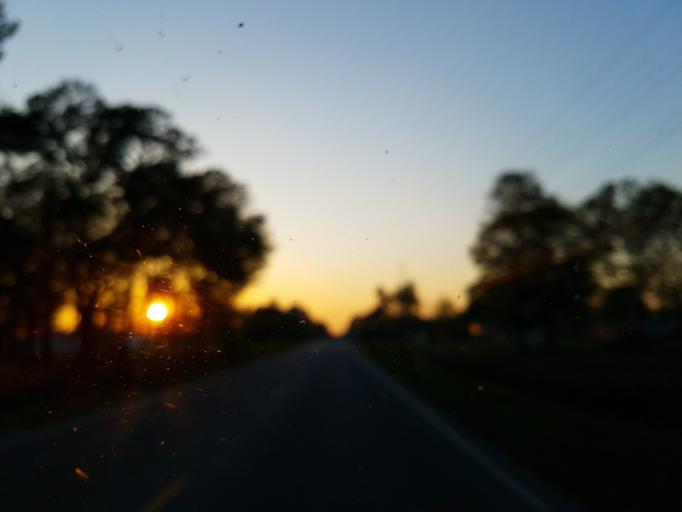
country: US
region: Georgia
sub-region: Lanier County
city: Lakeland
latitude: 31.0500
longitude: -83.1259
